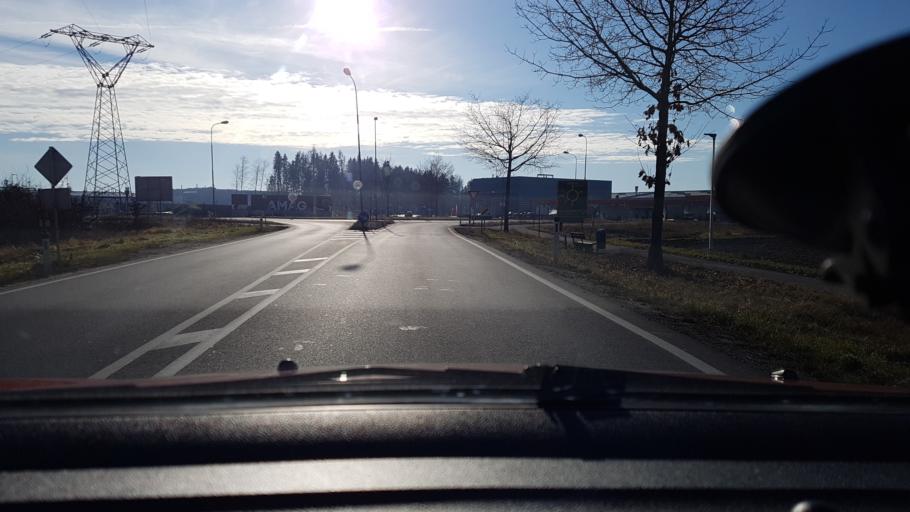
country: AT
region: Upper Austria
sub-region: Politischer Bezirk Braunau am Inn
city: Braunau am Inn
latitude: 48.2353
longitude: 13.0322
